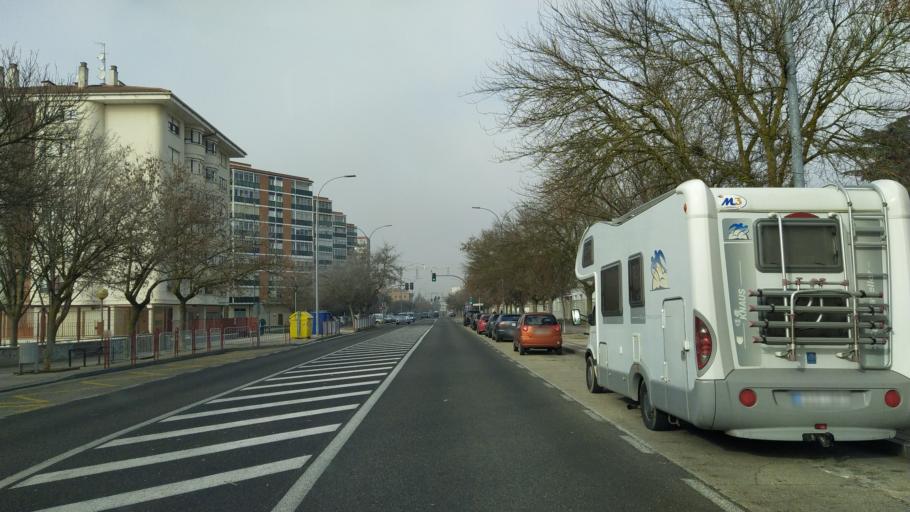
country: ES
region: Castille and Leon
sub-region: Provincia de Palencia
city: Palencia
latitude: 41.9959
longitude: -4.5189
